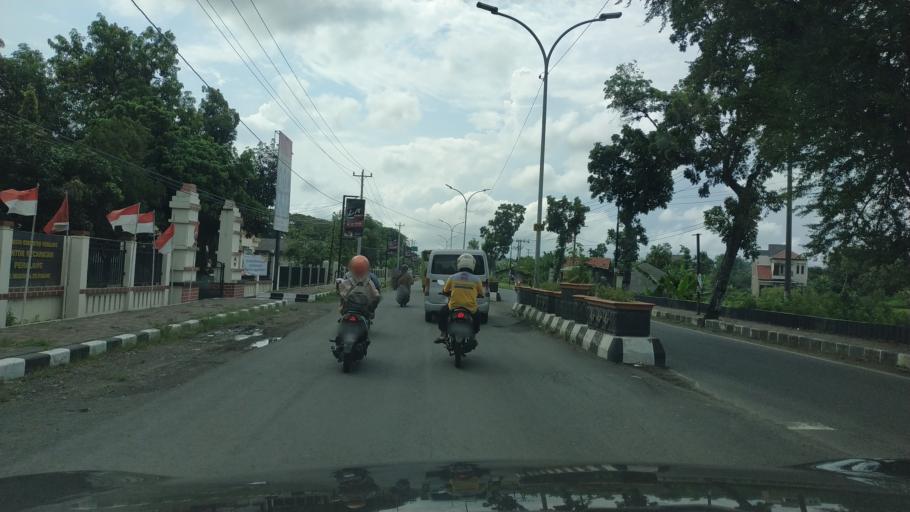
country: ID
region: Central Java
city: Pemalang
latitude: -6.9226
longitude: 109.3852
